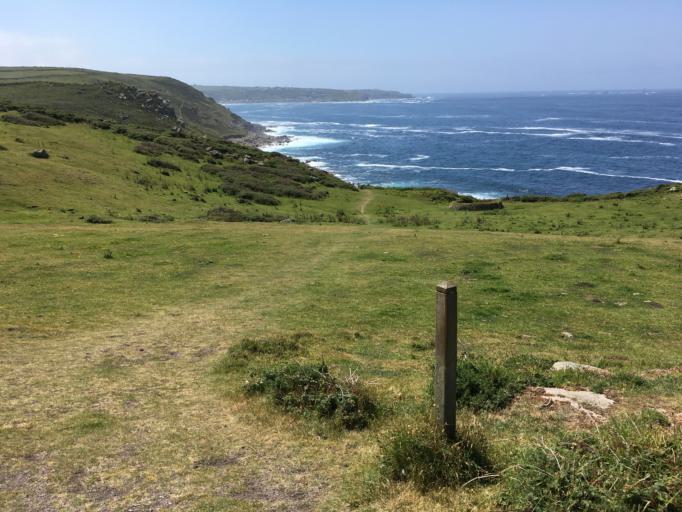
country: GB
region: England
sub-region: Cornwall
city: Saint Just
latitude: 50.1076
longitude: -5.6964
